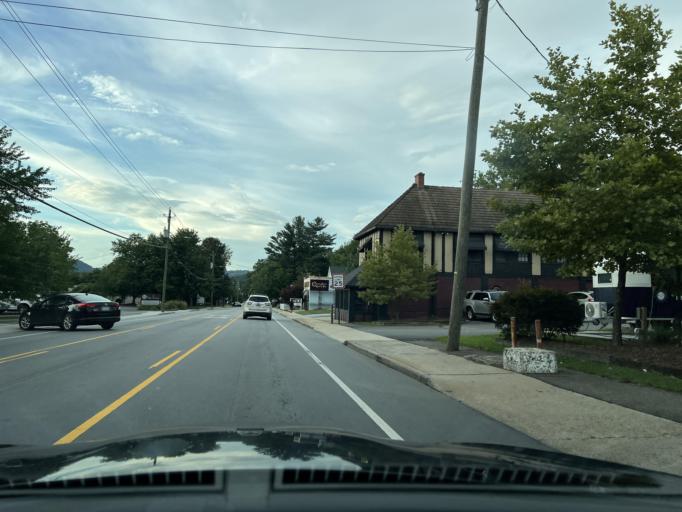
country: US
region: North Carolina
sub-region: Buncombe County
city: Asheville
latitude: 35.6046
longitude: -82.5465
